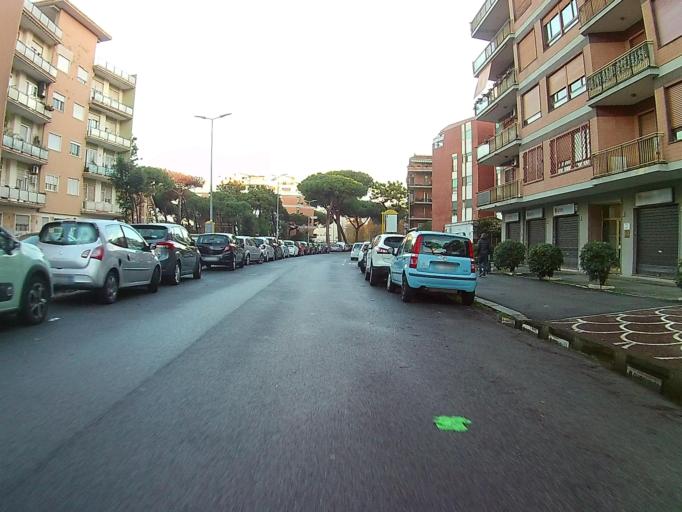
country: IT
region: Latium
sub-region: Citta metropolitana di Roma Capitale
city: Lido di Ostia
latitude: 41.7290
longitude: 12.2912
